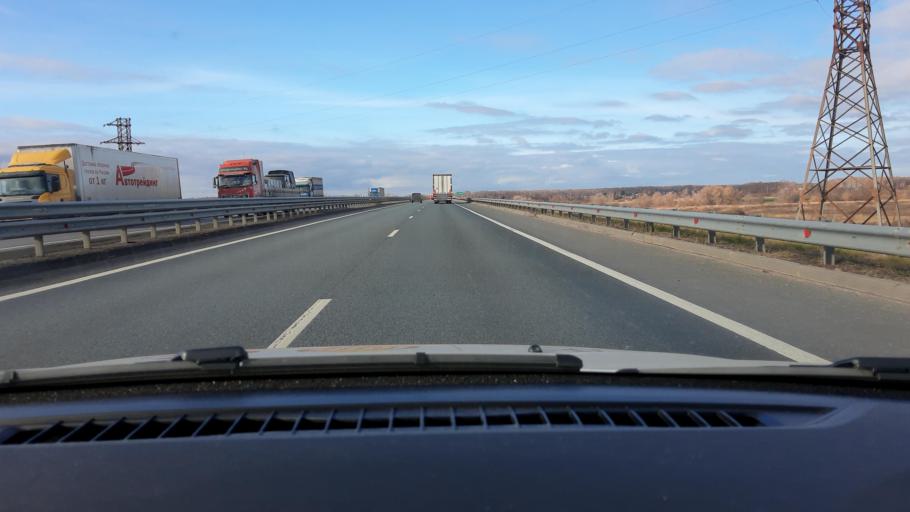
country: RU
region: Nizjnij Novgorod
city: Burevestnik
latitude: 56.1143
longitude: 43.8631
